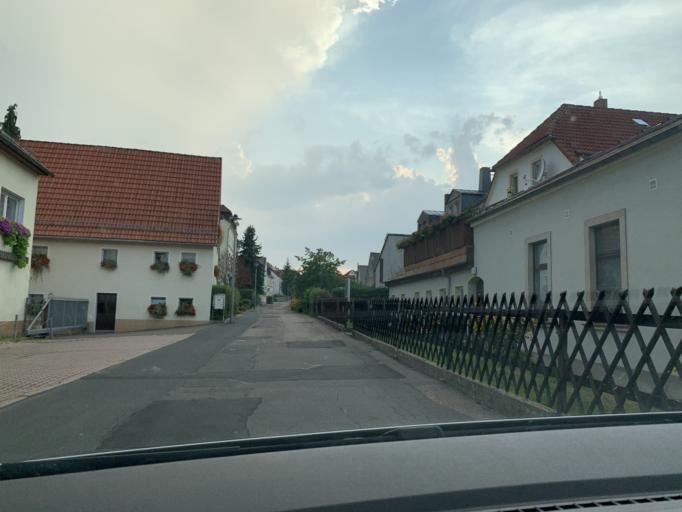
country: DE
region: Saxony
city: Freiberg
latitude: 50.9124
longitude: 13.3320
